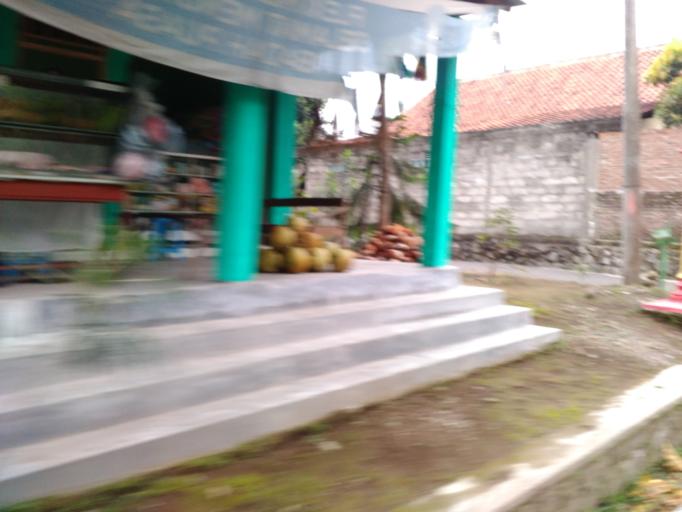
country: ID
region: Central Java
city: Boyolali
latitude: -7.5427
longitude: 110.6054
